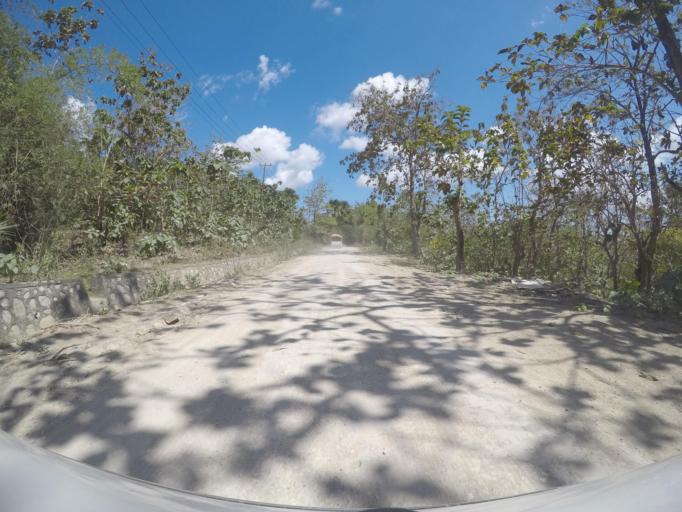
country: TL
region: Viqueque
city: Viqueque
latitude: -8.8913
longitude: 126.3868
